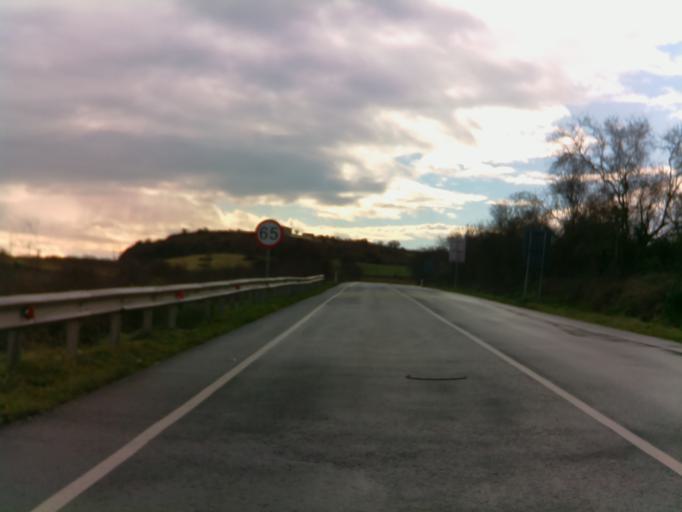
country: CY
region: Pafos
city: Pegeia
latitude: 34.9103
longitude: 32.4359
